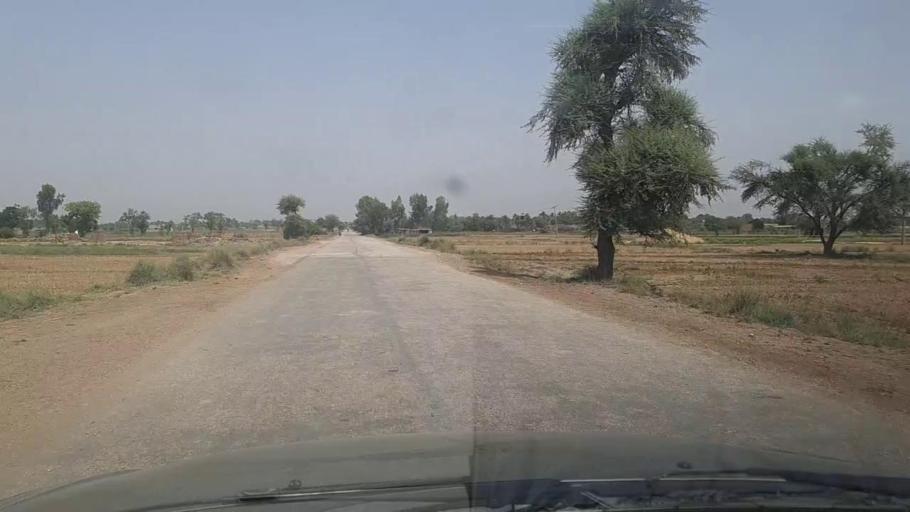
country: PK
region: Sindh
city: Setharja Old
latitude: 27.1583
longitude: 68.5199
